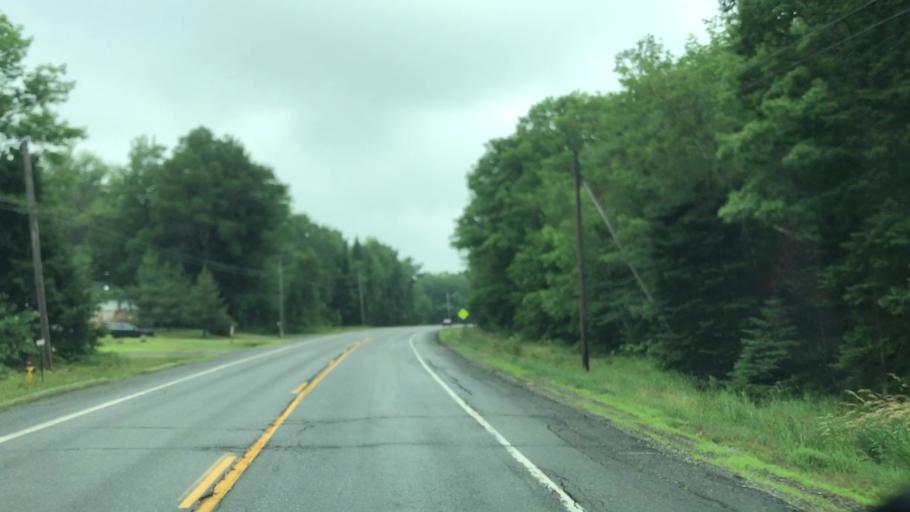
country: US
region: Maine
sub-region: Penobscot County
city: Howland
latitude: 45.2683
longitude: -68.6387
